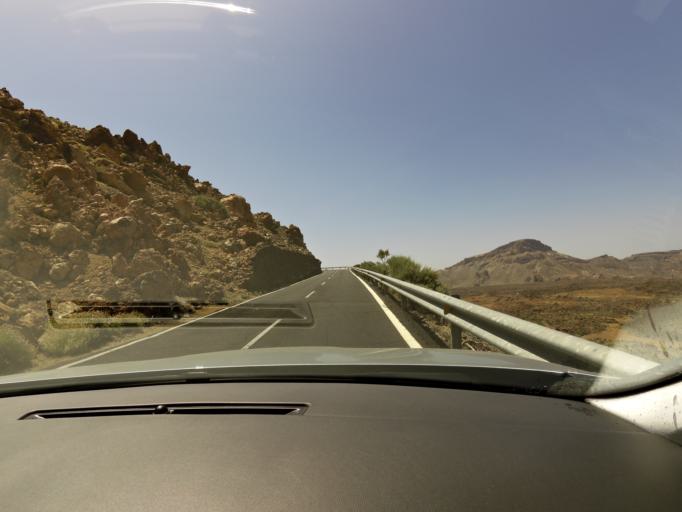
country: ES
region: Canary Islands
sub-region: Provincia de Santa Cruz de Tenerife
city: Vilaflor
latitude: 28.2585
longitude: -16.6130
